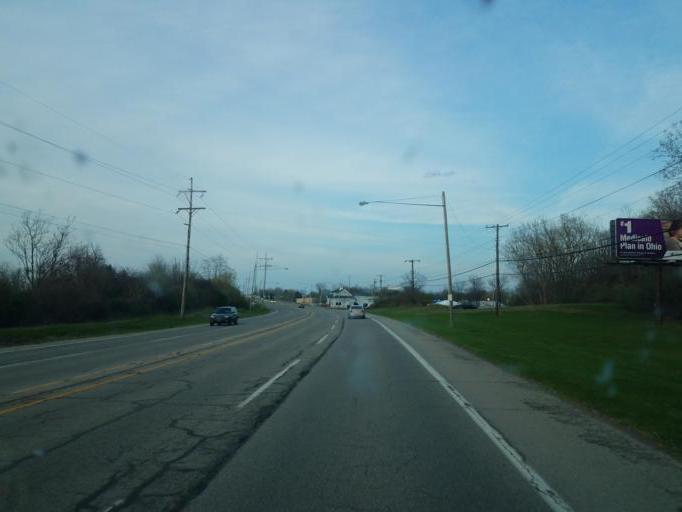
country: US
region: Ohio
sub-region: Lorain County
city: Amherst
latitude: 41.4346
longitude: -82.2515
